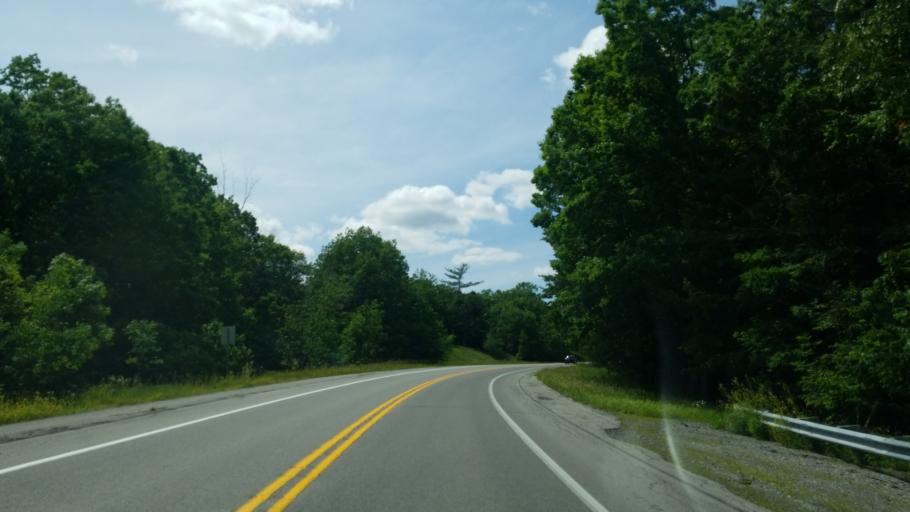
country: US
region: Pennsylvania
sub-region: Blair County
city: Tyrone
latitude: 40.6815
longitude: -78.2606
